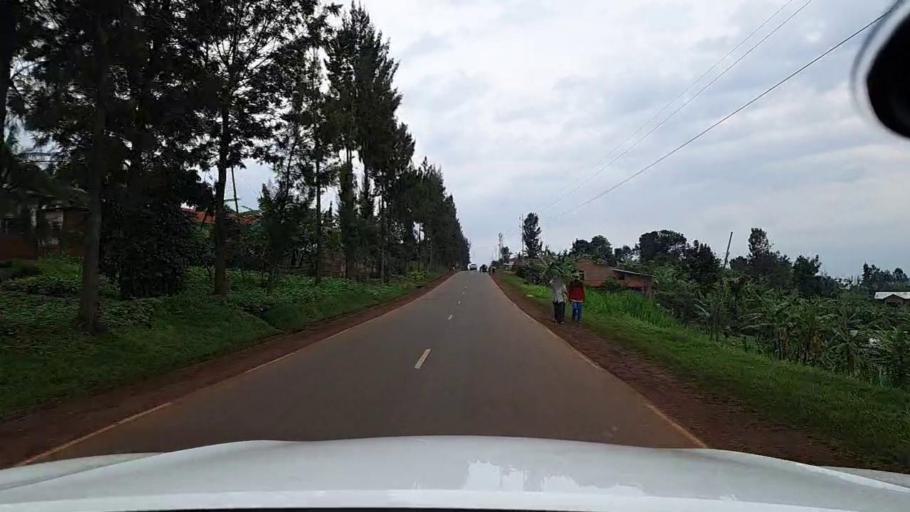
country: RW
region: Western Province
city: Cyangugu
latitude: -2.6228
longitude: 28.9472
